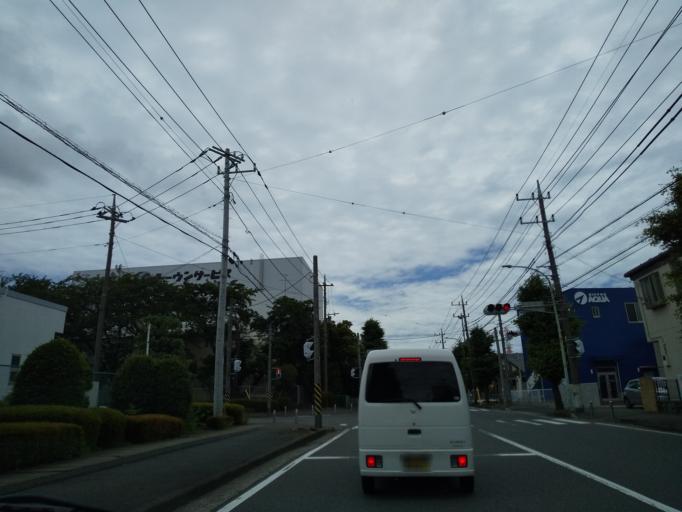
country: JP
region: Kanagawa
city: Zama
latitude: 35.5156
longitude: 139.3562
